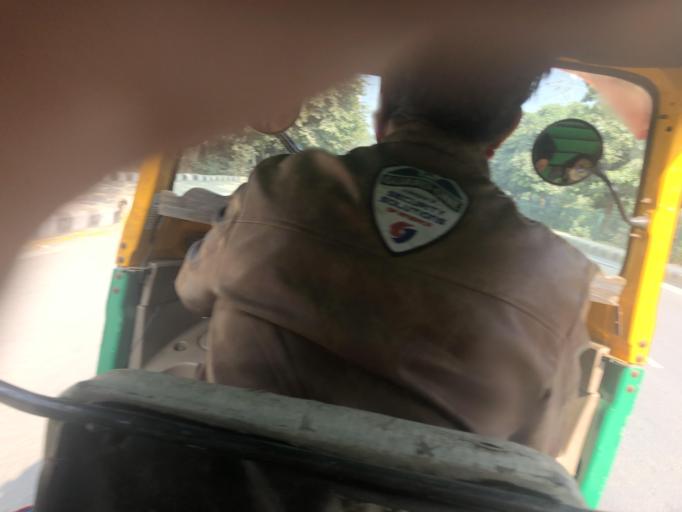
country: IN
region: Haryana
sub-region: Gurgaon
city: Gurgaon
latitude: 28.4284
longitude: 77.0912
